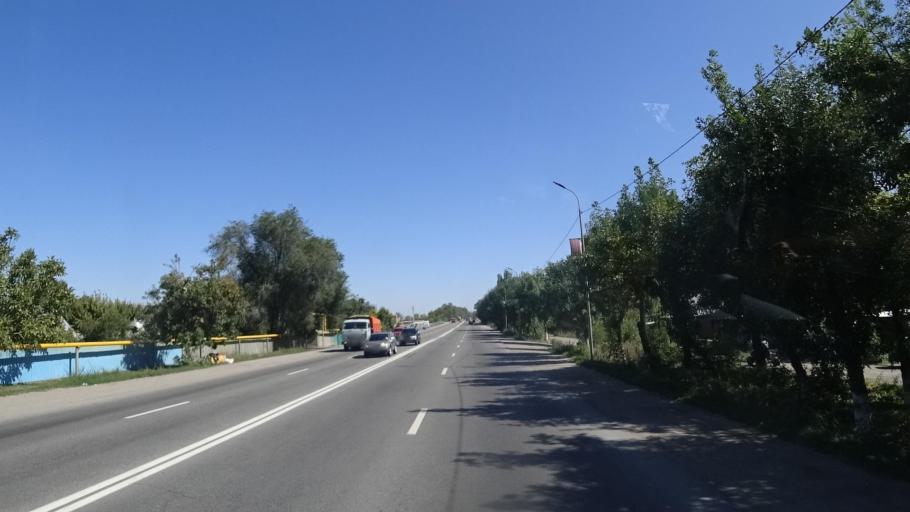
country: KZ
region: Almaty Oblysy
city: Energeticheskiy
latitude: 43.3902
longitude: 77.1258
